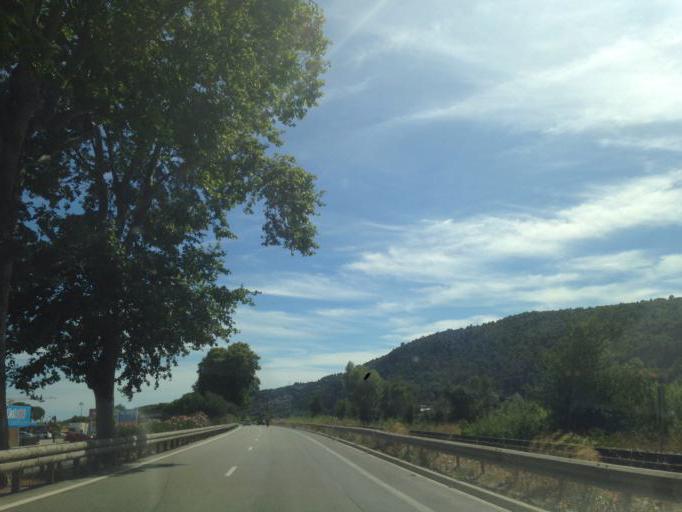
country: FR
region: Provence-Alpes-Cote d'Azur
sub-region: Departement des Alpes-Maritimes
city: Gattieres
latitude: 43.7433
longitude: 7.1855
